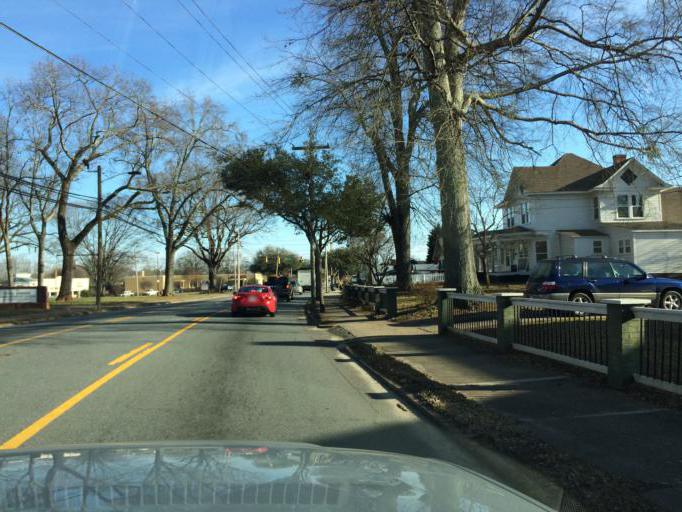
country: US
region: North Carolina
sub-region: Rutherford County
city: Forest City
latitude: 35.3384
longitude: -81.8734
